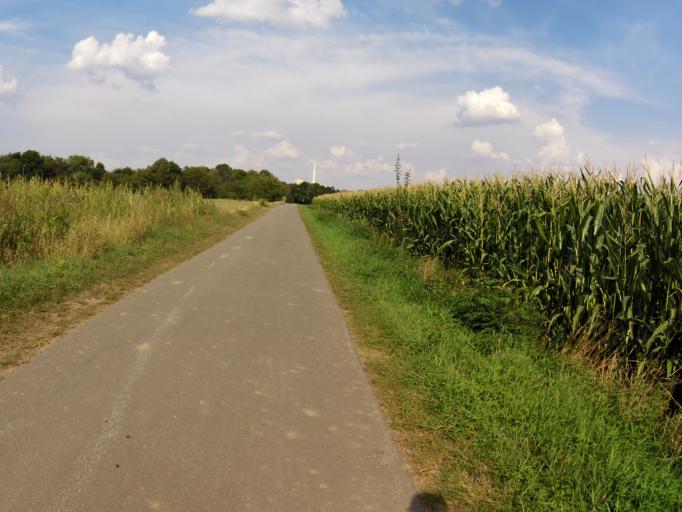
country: DE
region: North Rhine-Westphalia
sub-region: Regierungsbezirk Detmold
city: Petershagen
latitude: 52.3636
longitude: 8.9748
